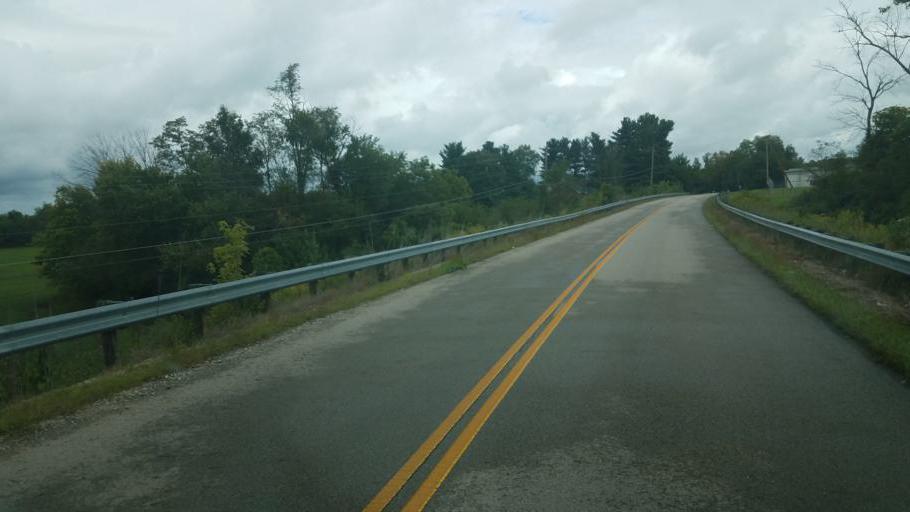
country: US
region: Ohio
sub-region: Scioto County
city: Wheelersburg
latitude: 38.7191
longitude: -82.8630
